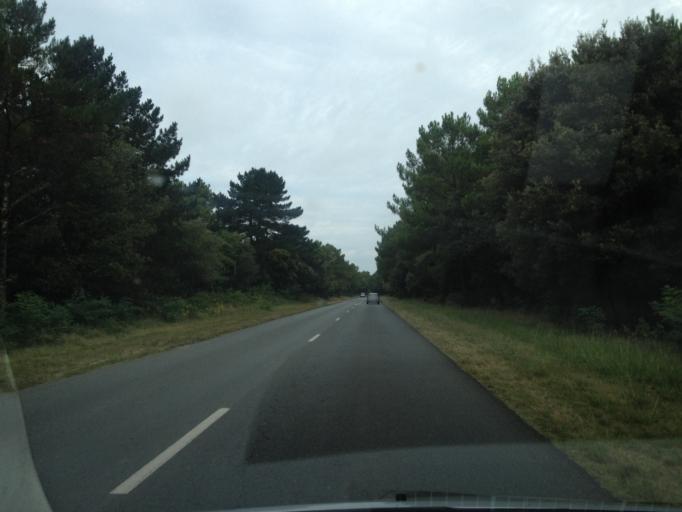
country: FR
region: Poitou-Charentes
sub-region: Departement de la Charente-Maritime
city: Les Mathes
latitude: 45.6777
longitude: -1.1513
